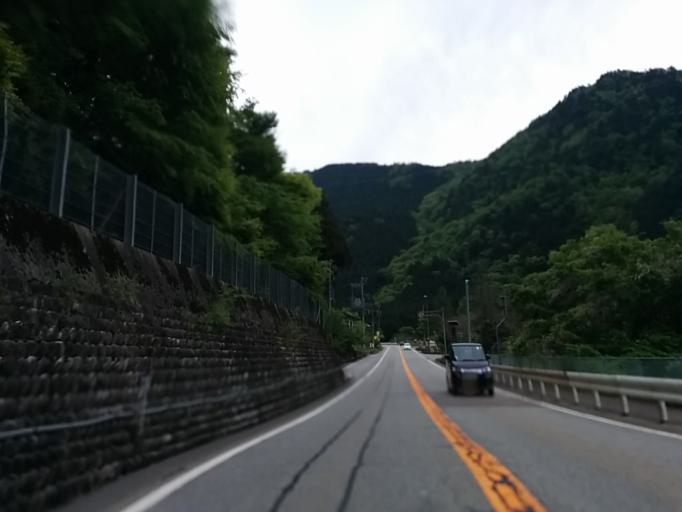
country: JP
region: Gifu
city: Gujo
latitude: 35.7506
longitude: 137.2138
